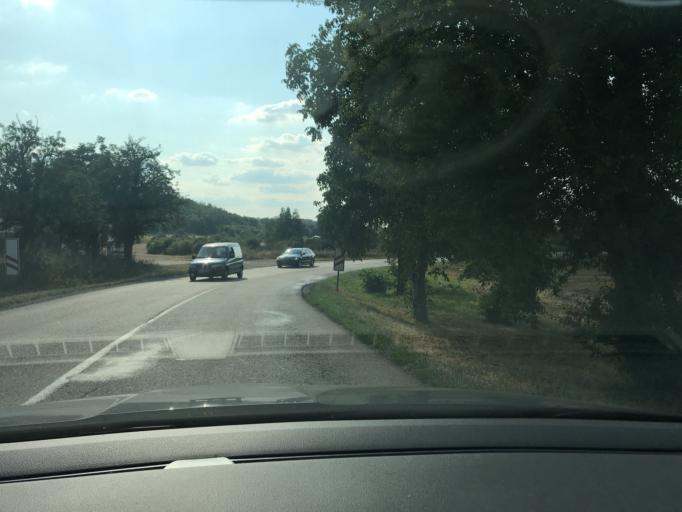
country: CZ
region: Central Bohemia
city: Kralupy nad Vltavou
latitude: 50.2307
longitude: 14.2820
